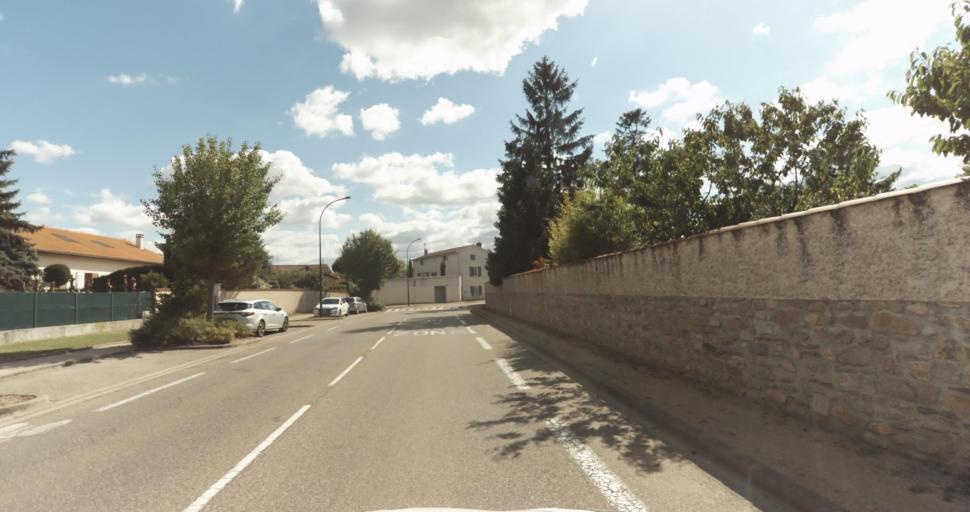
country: FR
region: Rhone-Alpes
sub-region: Departement du Rhone
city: Chaponost
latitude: 45.7159
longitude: 4.7518
